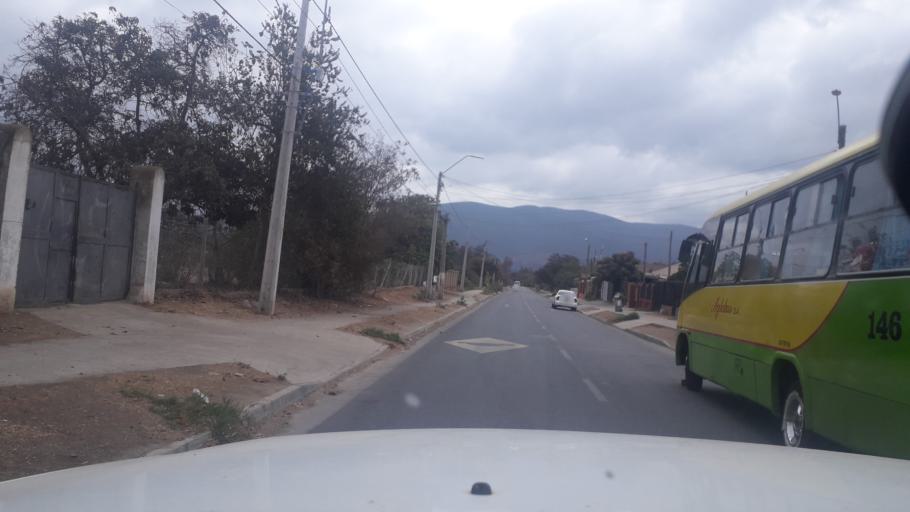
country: CL
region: Valparaiso
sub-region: Provincia de Marga Marga
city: Limache
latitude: -33.0177
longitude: -71.2691
